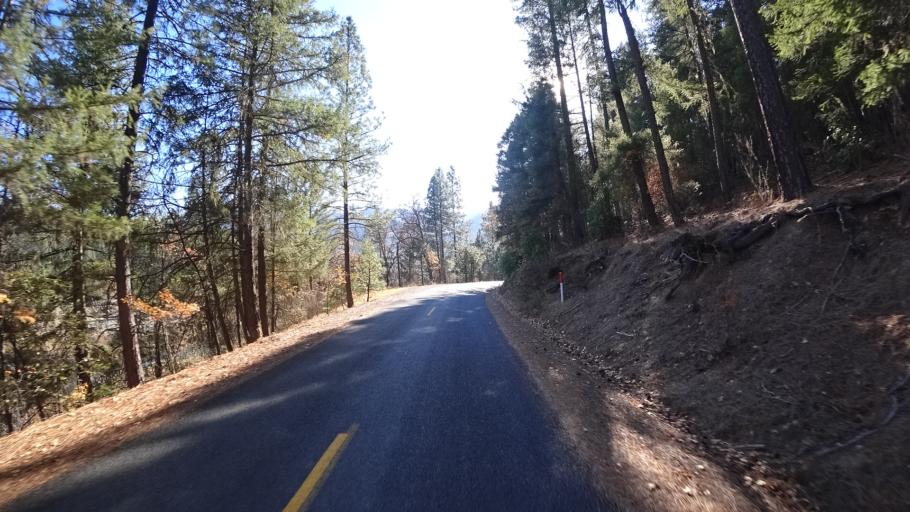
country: US
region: California
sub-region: Siskiyou County
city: Yreka
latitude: 41.8256
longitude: -122.9773
